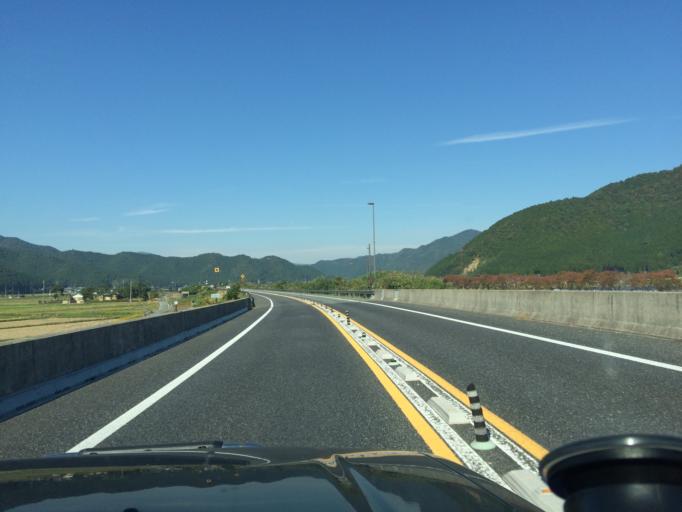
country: JP
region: Kyoto
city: Fukuchiyama
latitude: 35.2033
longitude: 135.0415
